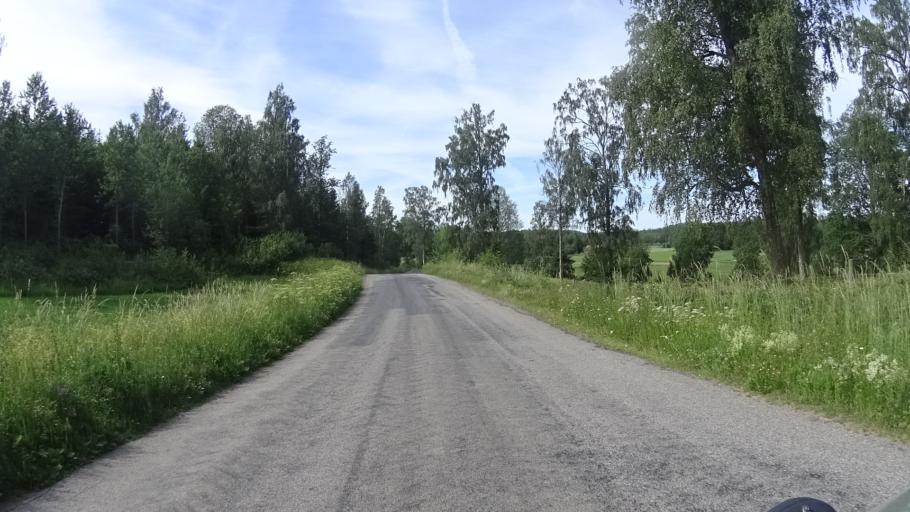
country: SE
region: Kalmar
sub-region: Vasterviks Kommun
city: Overum
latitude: 57.8780
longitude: 16.1762
